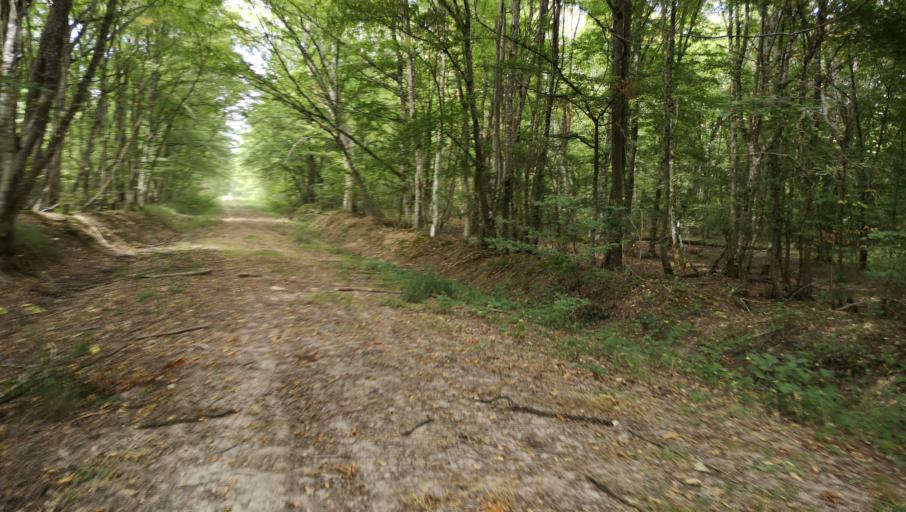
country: FR
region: Centre
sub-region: Departement du Loiret
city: Semoy
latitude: 47.9494
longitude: 1.9441
